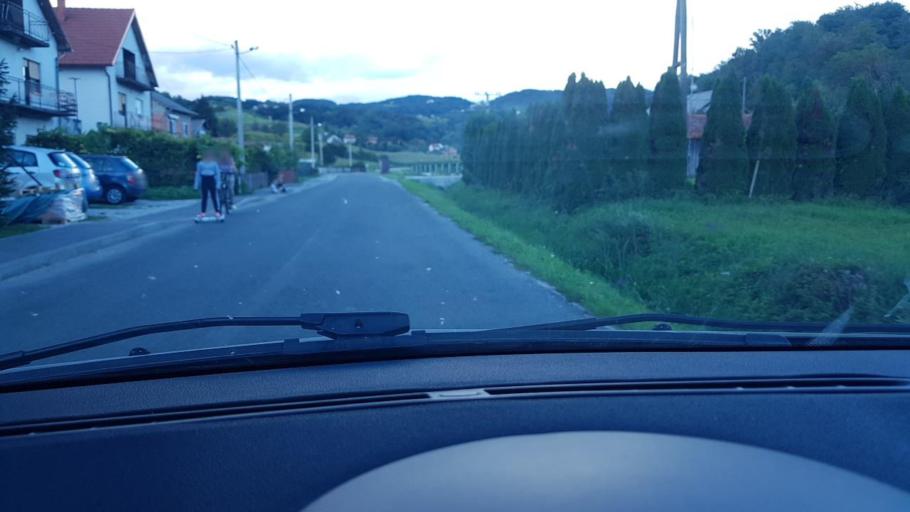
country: HR
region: Krapinsko-Zagorska
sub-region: Grad Krapina
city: Krapina
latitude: 46.1503
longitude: 15.8233
